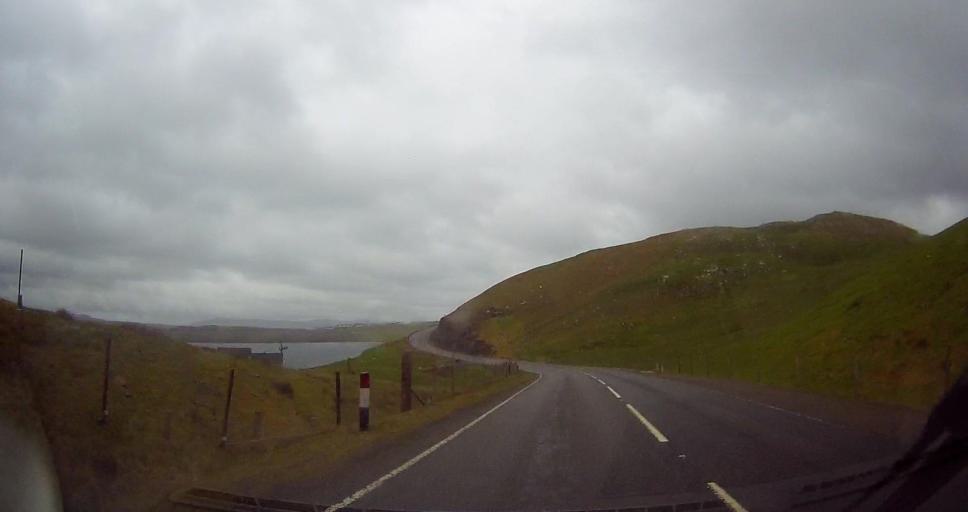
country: GB
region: Scotland
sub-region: Shetland Islands
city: Lerwick
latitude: 60.4048
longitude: -1.3859
